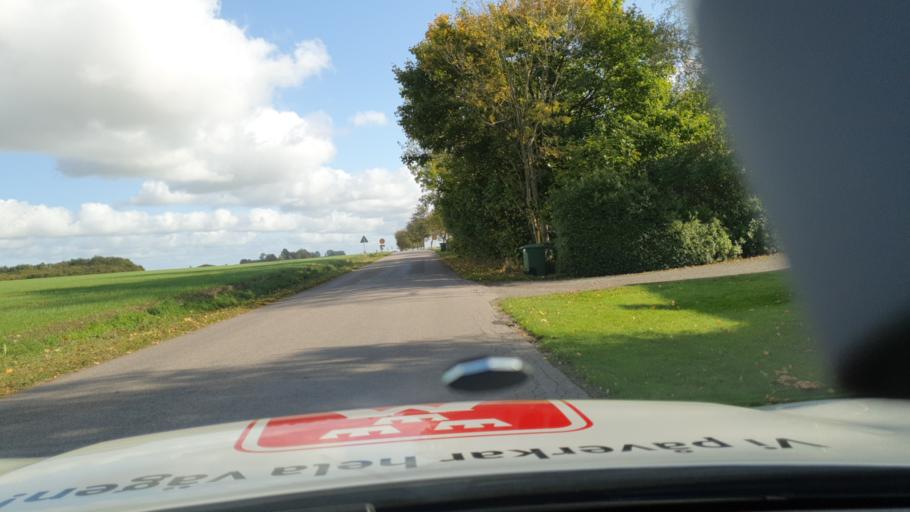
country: SE
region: Skane
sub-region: Tomelilla Kommun
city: Tomelilla
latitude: 55.5066
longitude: 13.9542
